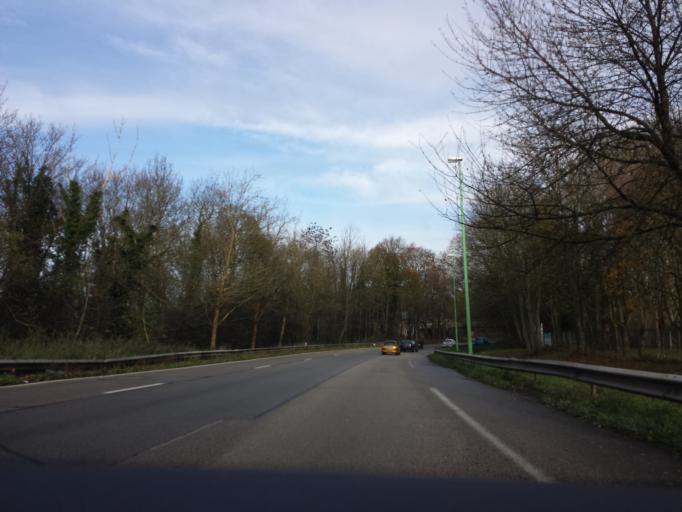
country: FR
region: Ile-de-France
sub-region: Departement des Yvelines
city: Fontenay-le-Fleury
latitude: 48.7973
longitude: 2.0448
